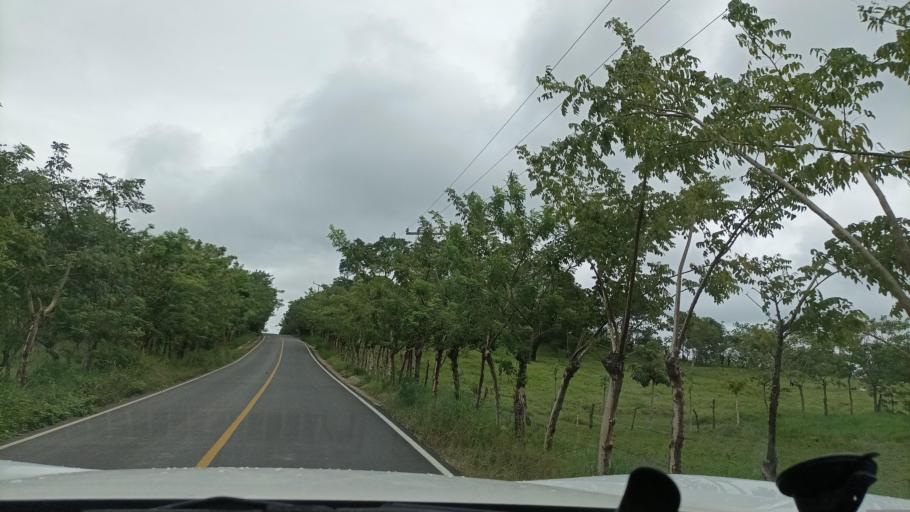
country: MX
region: Veracruz
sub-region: Moloacan
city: Cuichapa
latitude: 17.8018
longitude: -94.3575
